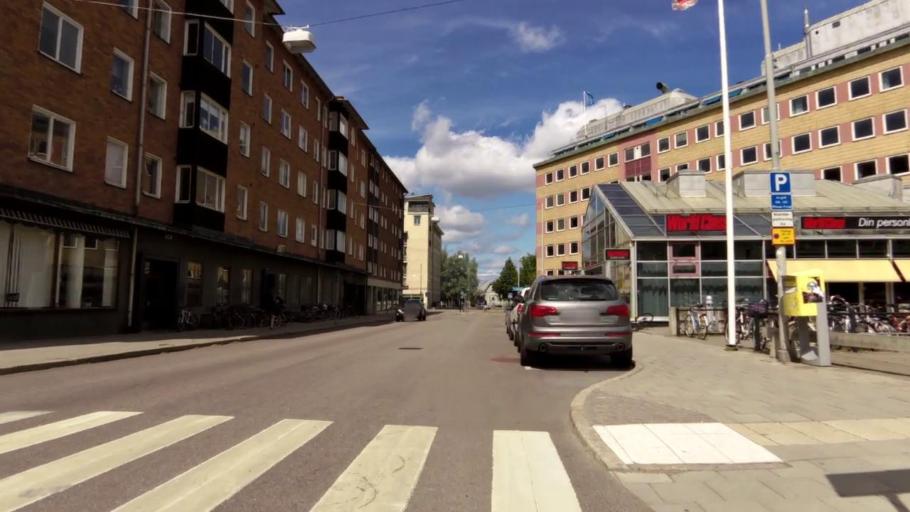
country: SE
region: OEstergoetland
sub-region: Linkopings Kommun
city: Linkoping
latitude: 58.4162
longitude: 15.6227
